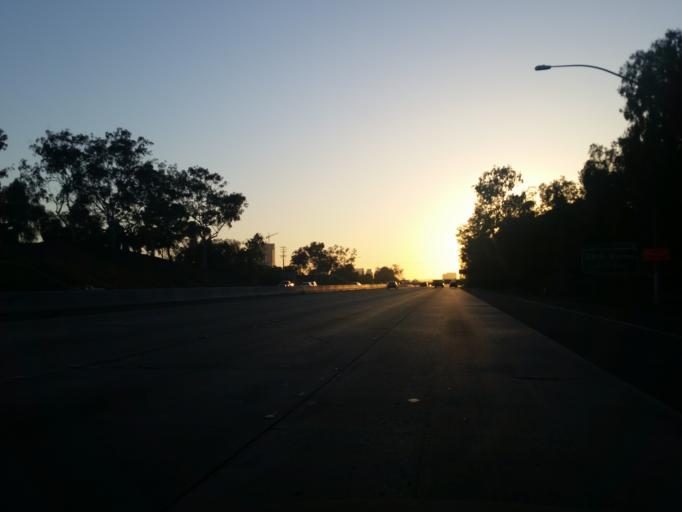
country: US
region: California
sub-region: San Diego County
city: San Diego
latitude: 32.7134
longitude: -117.1341
